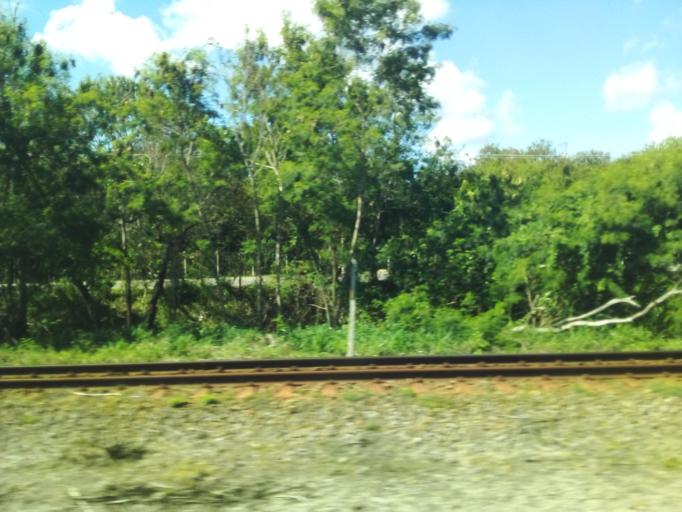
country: BR
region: Minas Gerais
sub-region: Governador Valadares
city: Governador Valadares
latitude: -18.8369
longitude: -41.8864
